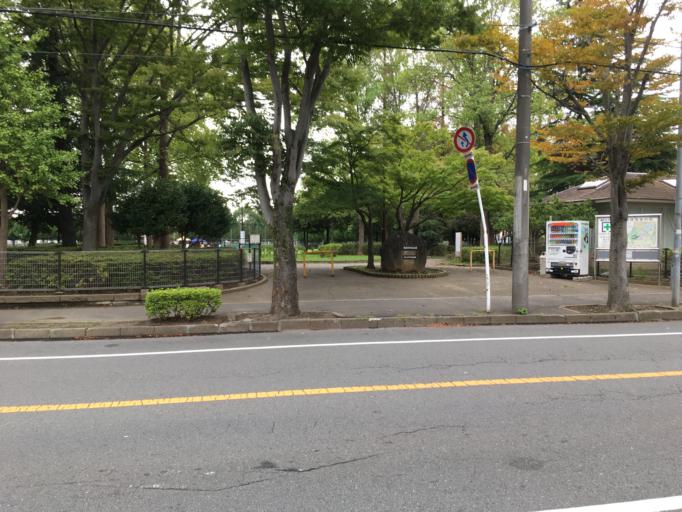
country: JP
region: Chiba
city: Nagareyama
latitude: 35.8339
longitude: 139.9138
